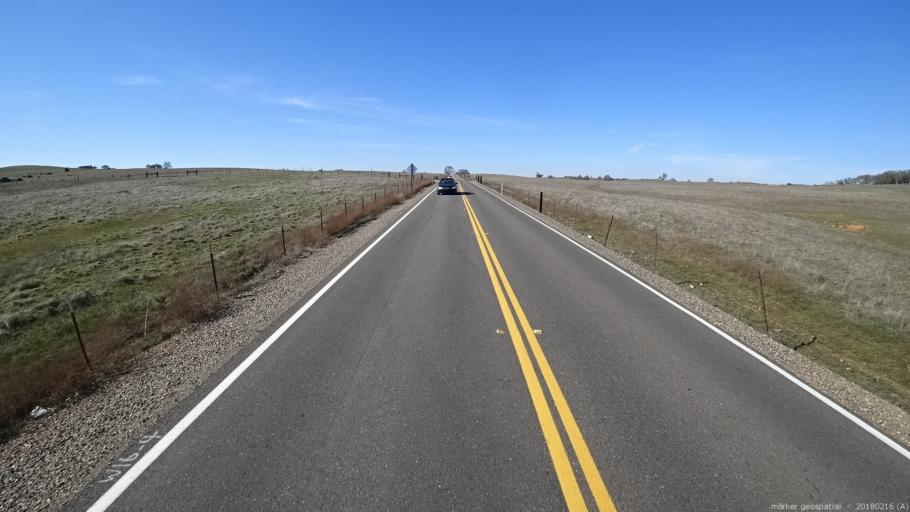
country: US
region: California
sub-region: Sacramento County
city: Rancho Murieta
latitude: 38.5564
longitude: -121.1176
